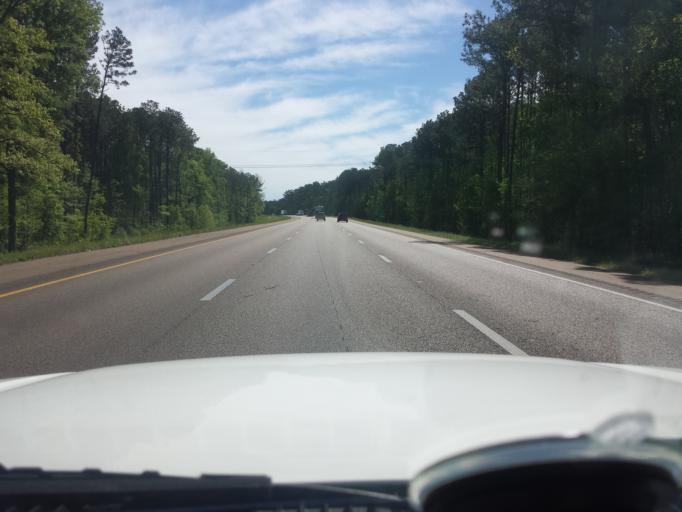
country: US
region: Mississippi
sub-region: Rankin County
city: Pearl
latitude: 32.2658
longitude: -90.1097
